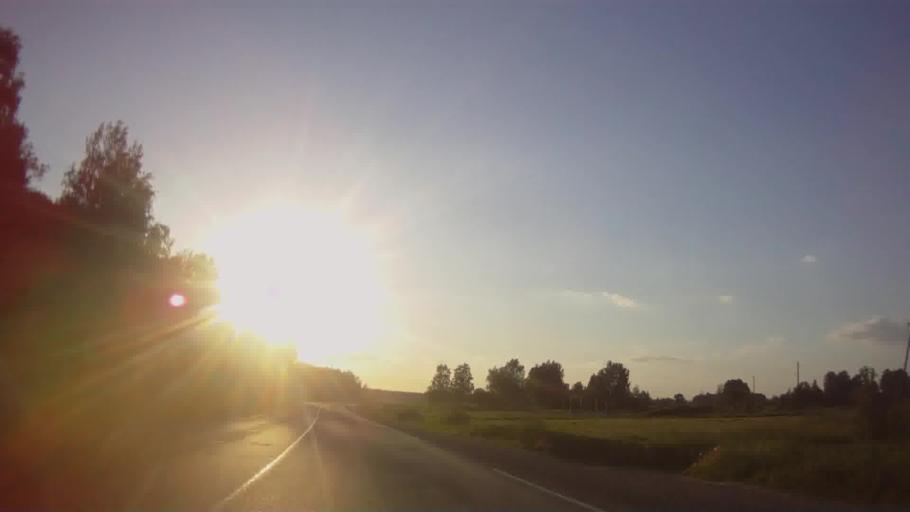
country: LV
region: Salas
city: Sala
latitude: 56.5490
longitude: 25.7999
